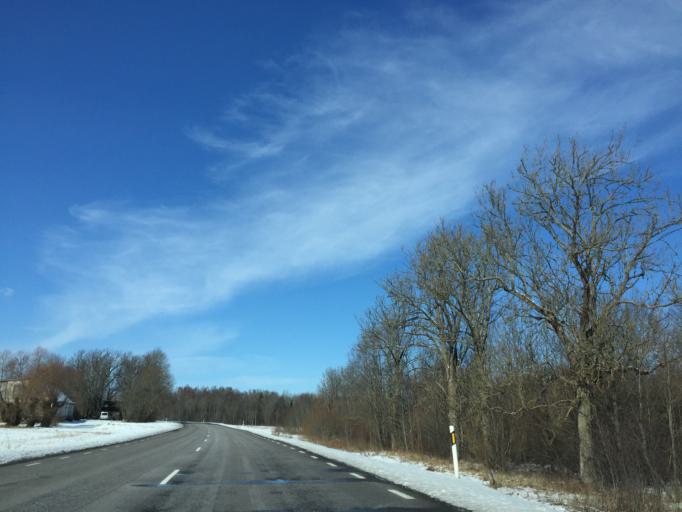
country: EE
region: Paernumaa
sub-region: Audru vald
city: Audru
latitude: 58.5055
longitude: 24.1154
